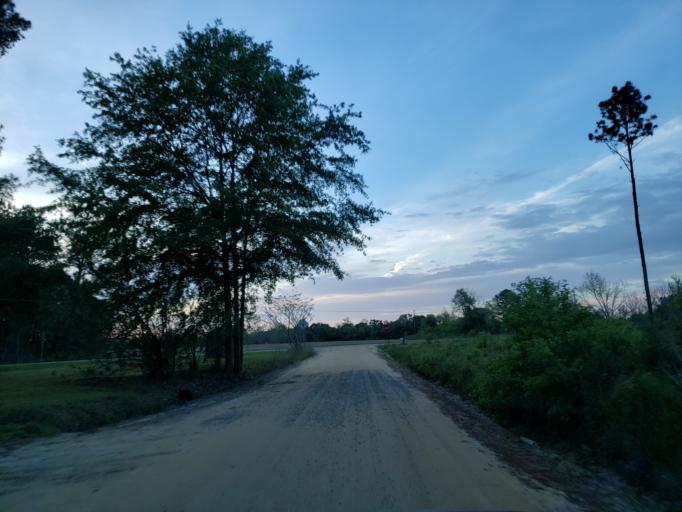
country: US
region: Georgia
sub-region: Lowndes County
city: Hahira
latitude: 30.9744
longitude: -83.3968
